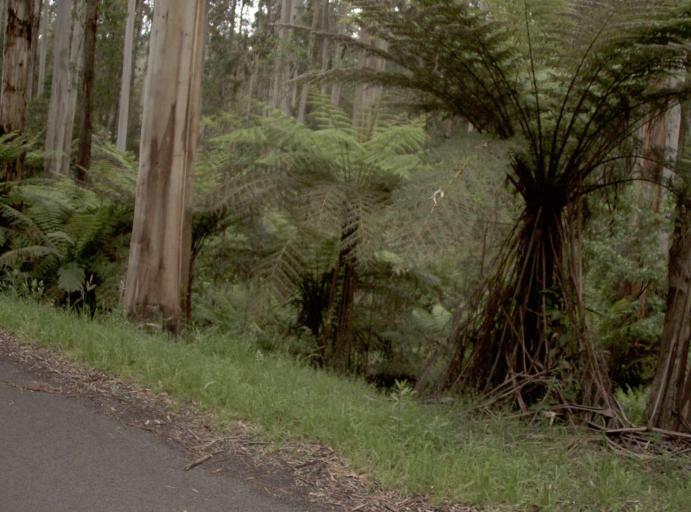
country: AU
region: Victoria
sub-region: Baw Baw
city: Warragul
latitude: -37.9281
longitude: 146.1079
